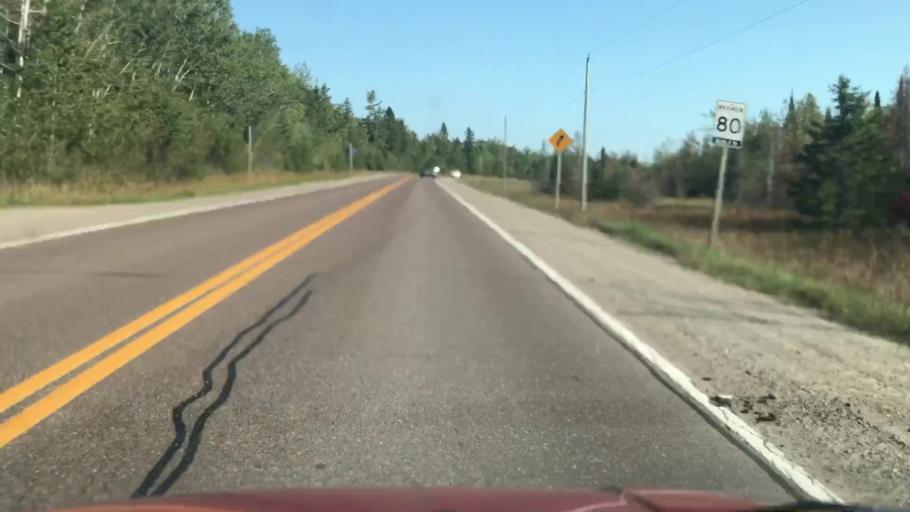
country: CA
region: Ontario
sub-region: Algoma
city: Sault Ste. Marie
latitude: 46.3359
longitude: -84.0079
